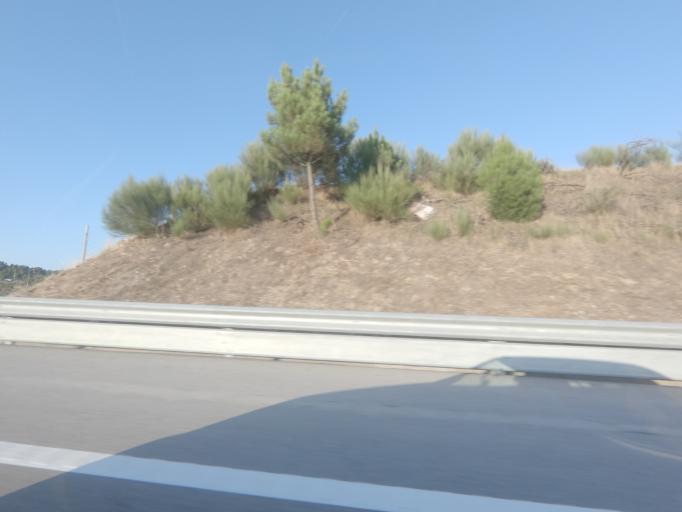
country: PT
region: Vila Real
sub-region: Vila Real
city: Vila Real
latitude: 41.2914
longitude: -7.6924
